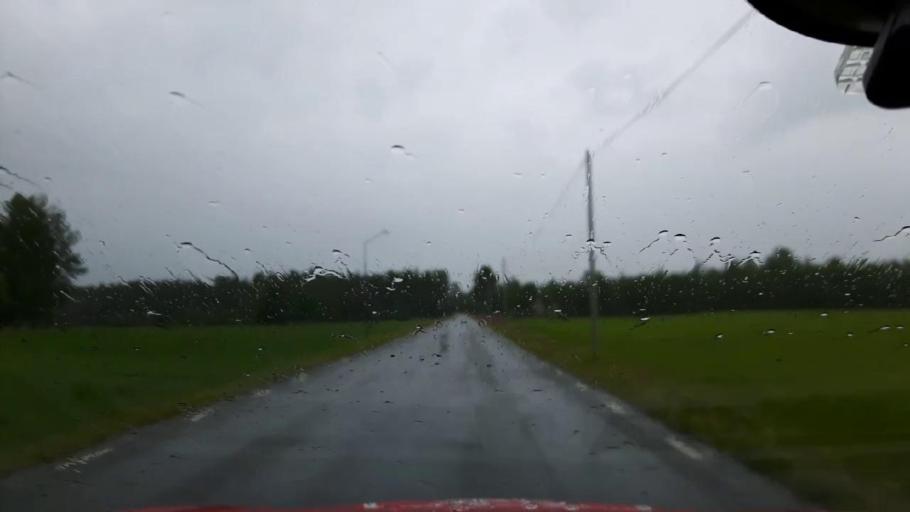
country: SE
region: Jaemtland
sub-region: OEstersunds Kommun
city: Brunflo
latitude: 62.9919
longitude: 14.7936
